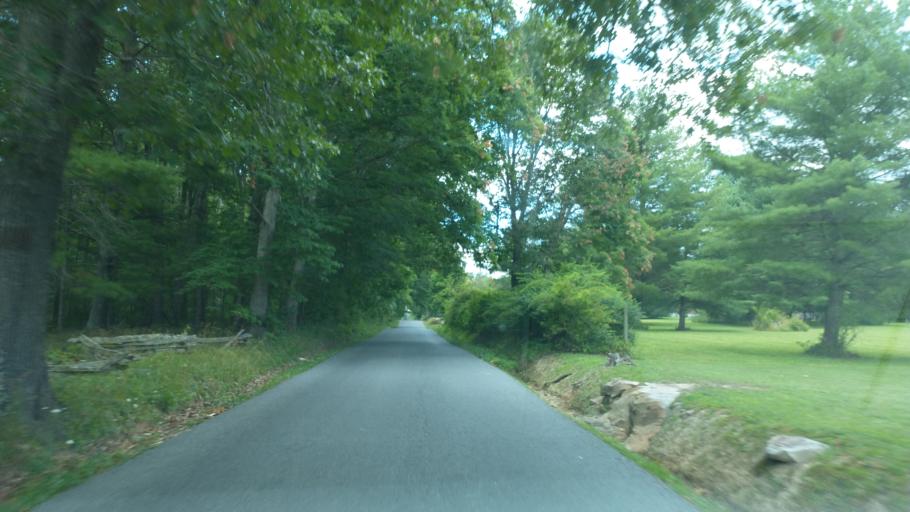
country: US
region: West Virginia
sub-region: Mercer County
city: Athens
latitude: 37.4579
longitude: -81.0443
